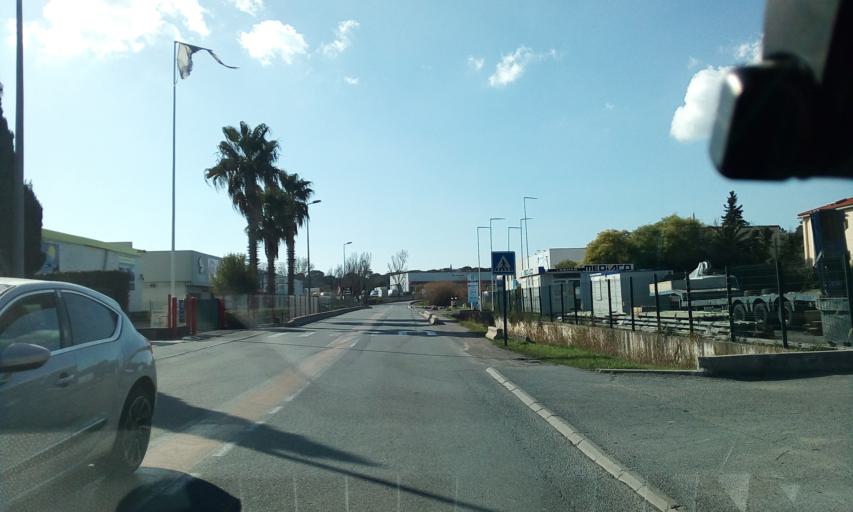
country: FR
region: Provence-Alpes-Cote d'Azur
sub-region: Departement du Var
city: Frejus
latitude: 43.4699
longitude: 6.7348
